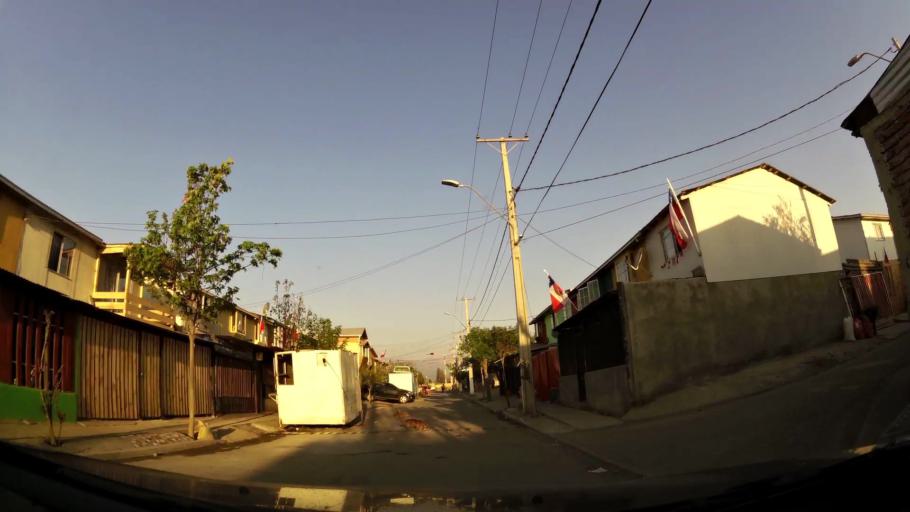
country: CL
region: Santiago Metropolitan
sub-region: Provincia de Maipo
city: San Bernardo
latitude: -33.5913
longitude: -70.6695
